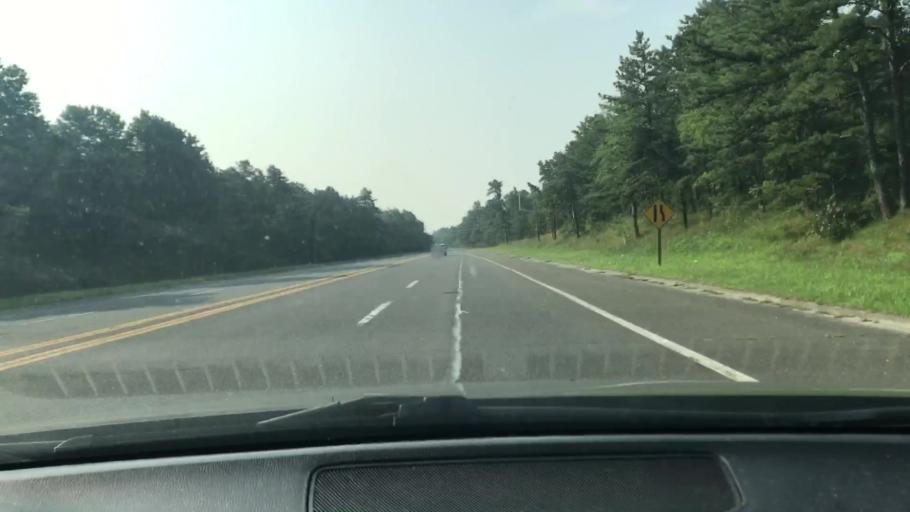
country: US
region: New York
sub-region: Suffolk County
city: Riverhead
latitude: 40.8950
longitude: -72.6480
